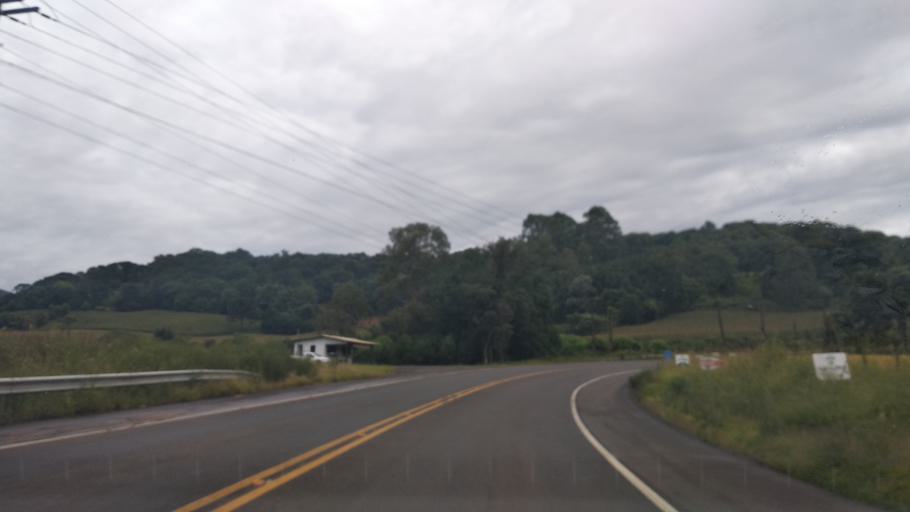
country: BR
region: Santa Catarina
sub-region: Videira
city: Videira
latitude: -27.0474
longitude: -51.1572
